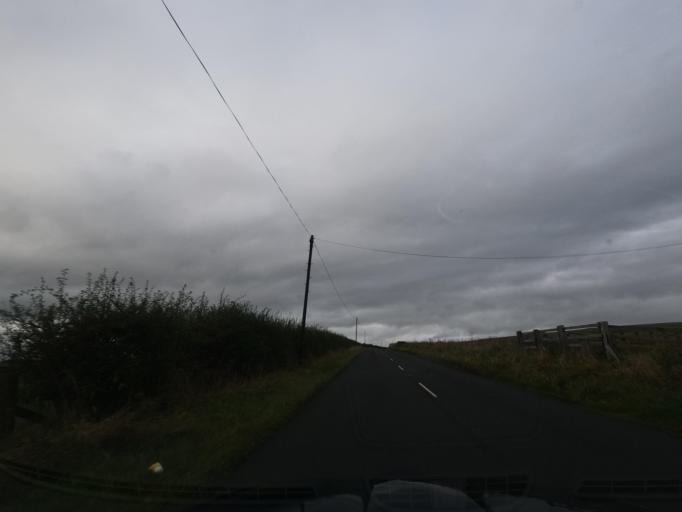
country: GB
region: England
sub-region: Northumberland
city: Doddington
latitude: 55.5935
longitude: -2.0027
